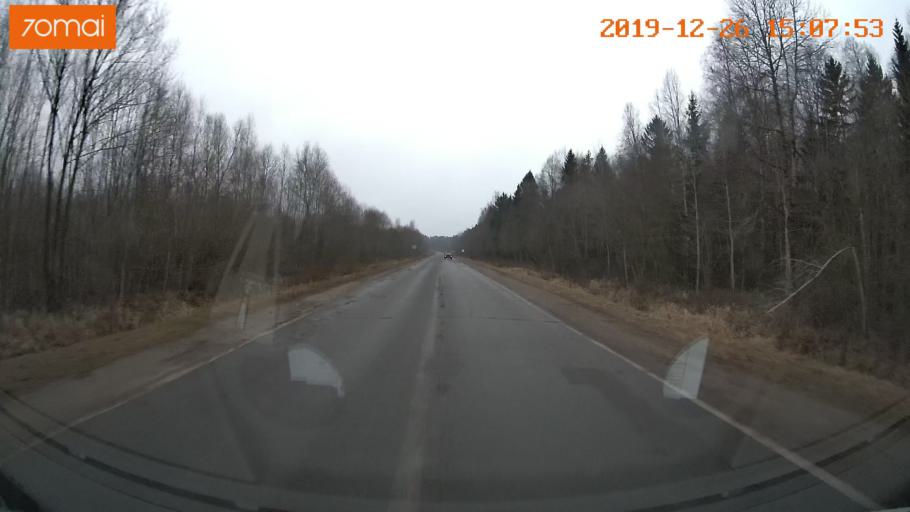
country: RU
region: Jaroslavl
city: Rybinsk
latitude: 58.1654
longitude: 38.8420
